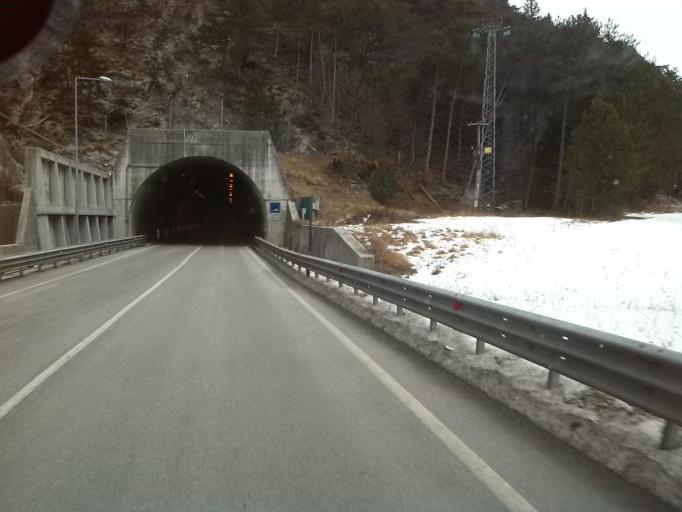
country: IT
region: Friuli Venezia Giulia
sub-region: Provincia di Udine
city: Malborghetto
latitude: 46.5029
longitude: 13.4052
